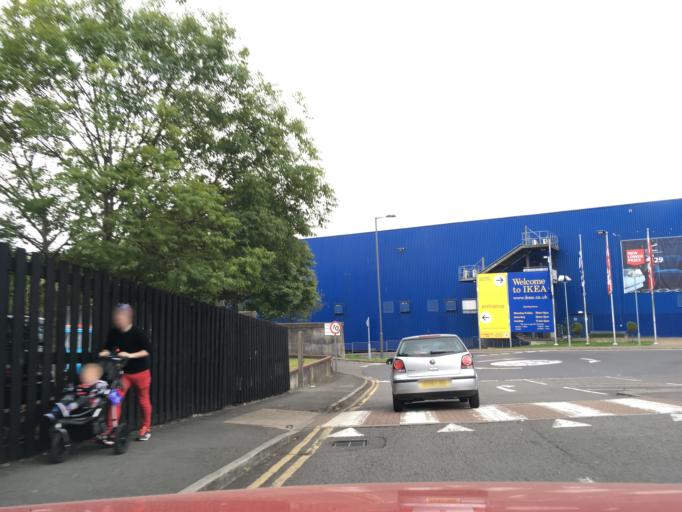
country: GB
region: England
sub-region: Bristol
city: Bristol
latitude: 51.4736
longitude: -2.5642
